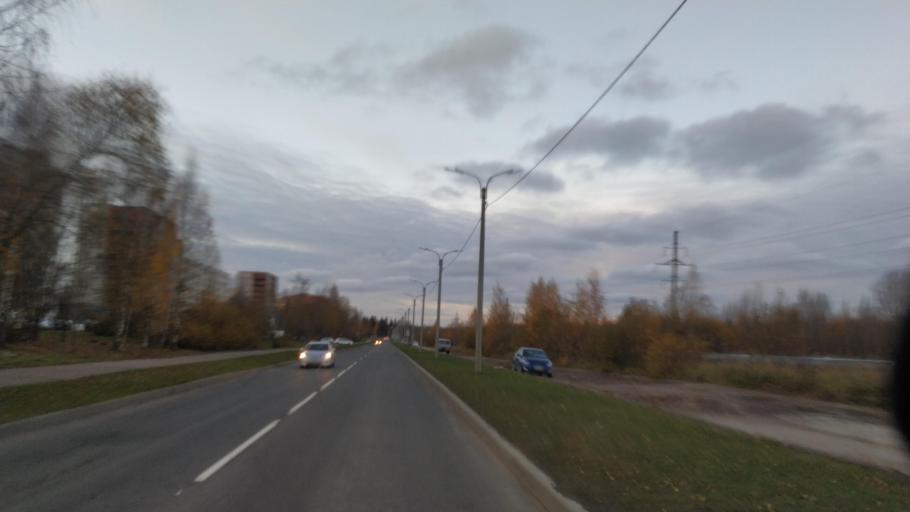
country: RU
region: Leningrad
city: Sosnovyy Bor
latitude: 59.9128
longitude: 29.0970
